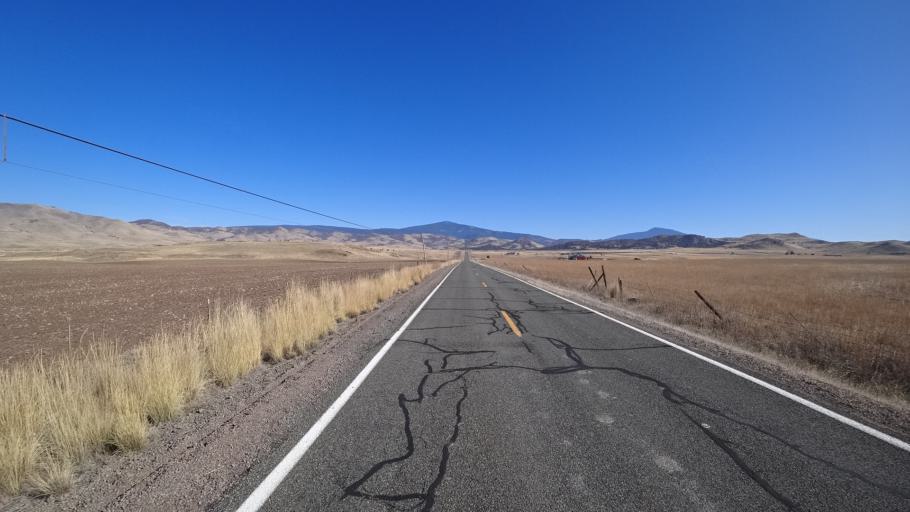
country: US
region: California
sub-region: Siskiyou County
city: Montague
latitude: 41.8082
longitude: -122.4351
